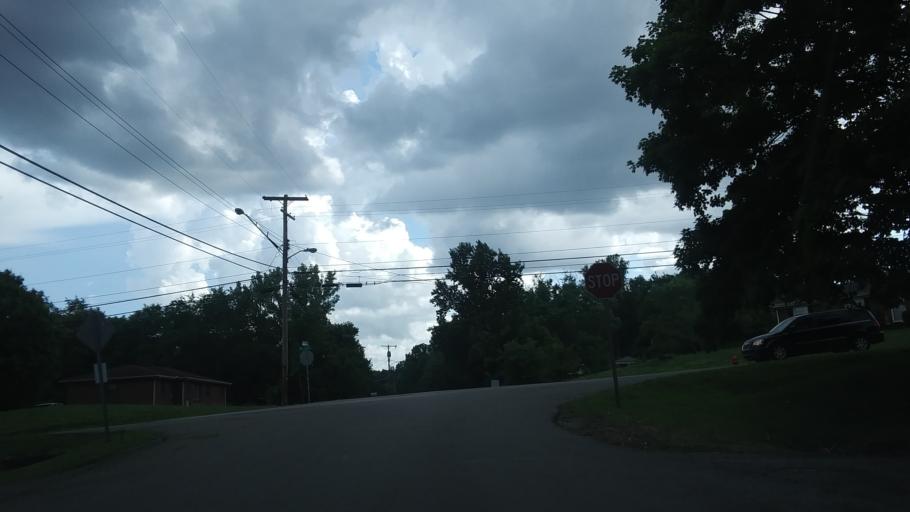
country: US
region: Tennessee
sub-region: Davidson County
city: Oak Hill
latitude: 36.0739
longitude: -86.7011
